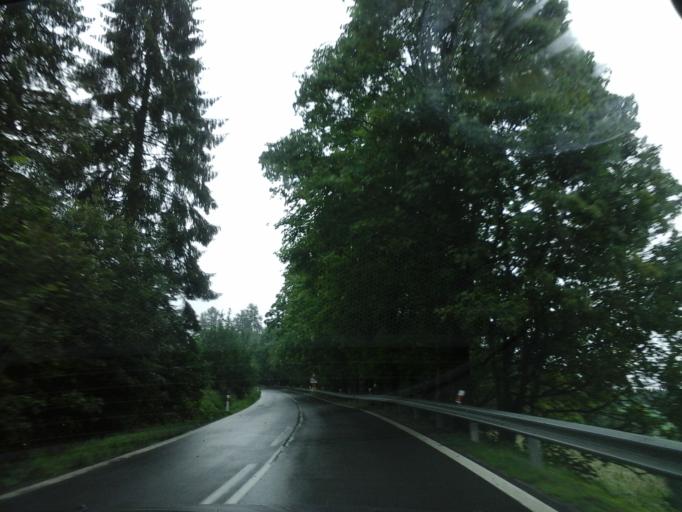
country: PL
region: Lesser Poland Voivodeship
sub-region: Powiat tatrzanski
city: Bukowina Tatrzanska
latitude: 49.2682
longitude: 20.1400
